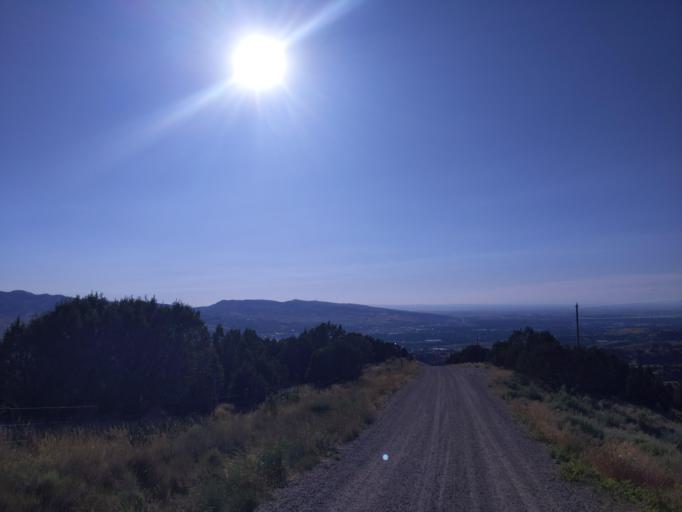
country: US
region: Idaho
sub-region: Bannock County
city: Pocatello
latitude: 42.8528
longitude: -112.3809
